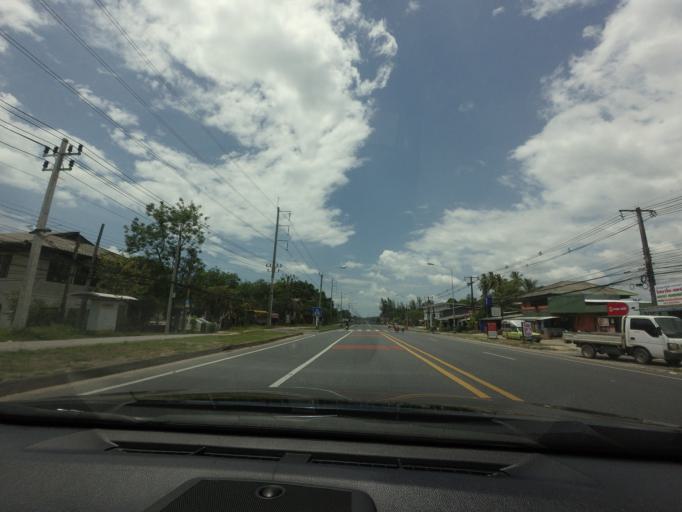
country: TH
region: Phangnga
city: Ban Khao Lak
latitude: 8.6580
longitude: 98.2534
